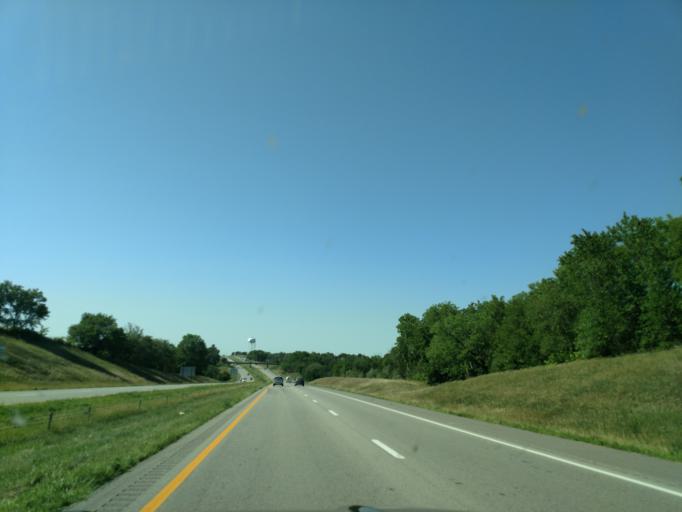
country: US
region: Missouri
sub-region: Andrew County
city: Country Club Village
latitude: 39.7861
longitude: -94.7950
